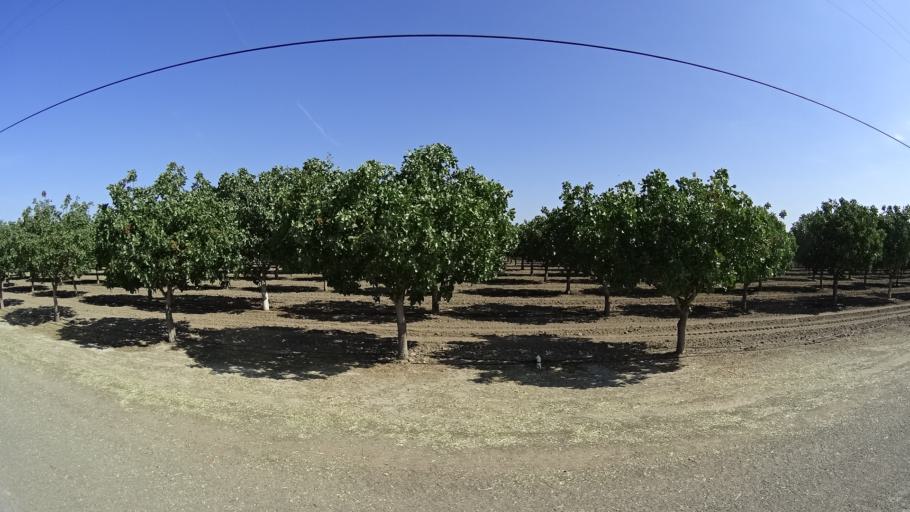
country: US
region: California
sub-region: Kings County
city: Home Garden
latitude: 36.2550
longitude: -119.5685
